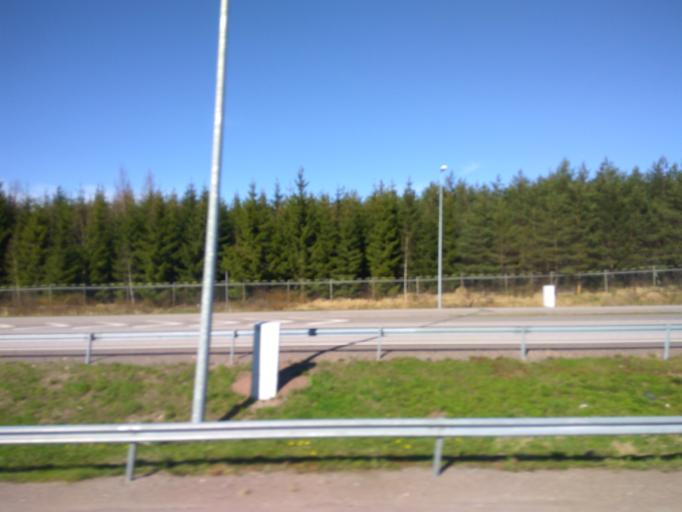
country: FI
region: Uusimaa
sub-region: Loviisa
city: Lovisa
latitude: 60.4627
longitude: 26.1456
